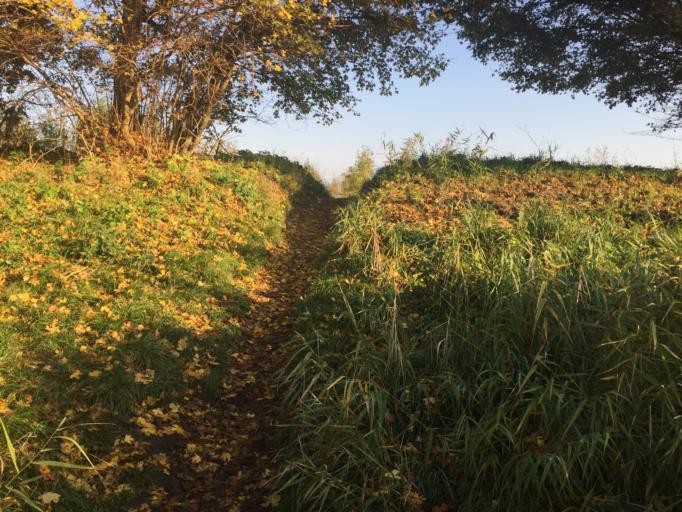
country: NL
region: South Holland
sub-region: Gemeente Lansingerland
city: Bergschenhoek
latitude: 52.0055
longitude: 4.5002
